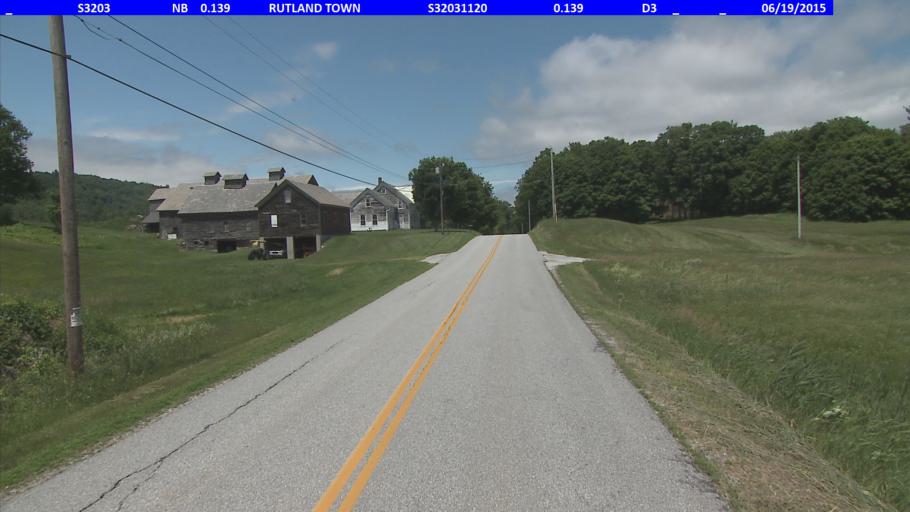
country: US
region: Vermont
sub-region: Rutland County
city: Rutland
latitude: 43.6556
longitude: -72.9966
